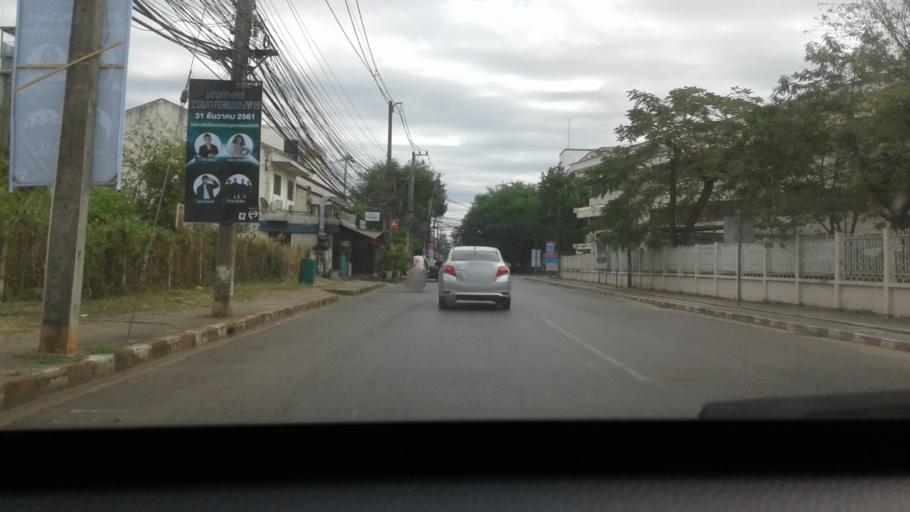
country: TH
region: Changwat Udon Thani
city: Udon Thani
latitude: 17.4188
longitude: 102.7865
